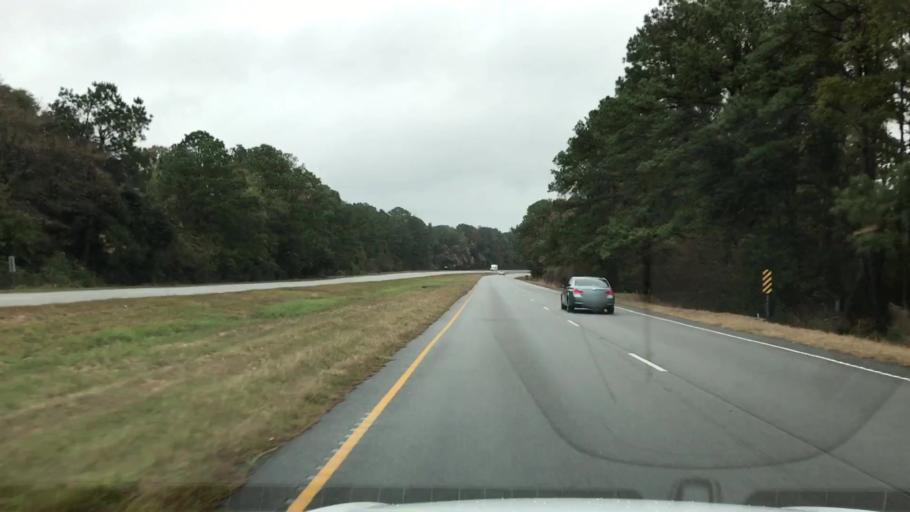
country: US
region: South Carolina
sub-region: Charleston County
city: Awendaw
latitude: 32.9335
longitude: -79.7126
